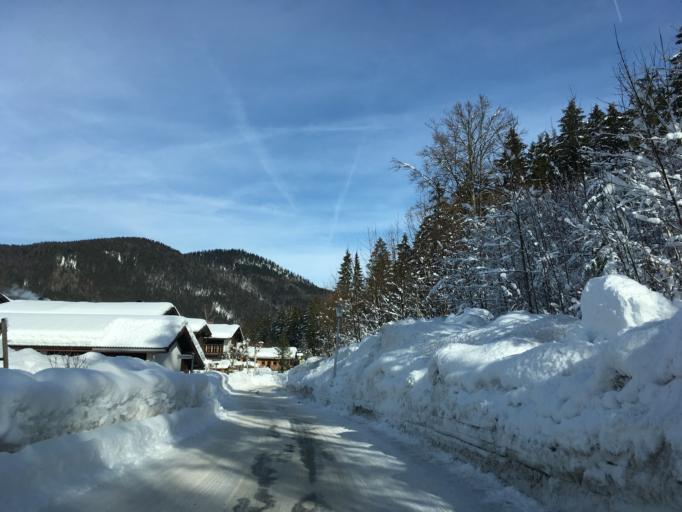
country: DE
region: Bavaria
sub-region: Upper Bavaria
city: Schliersee
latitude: 47.6954
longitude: 11.8920
